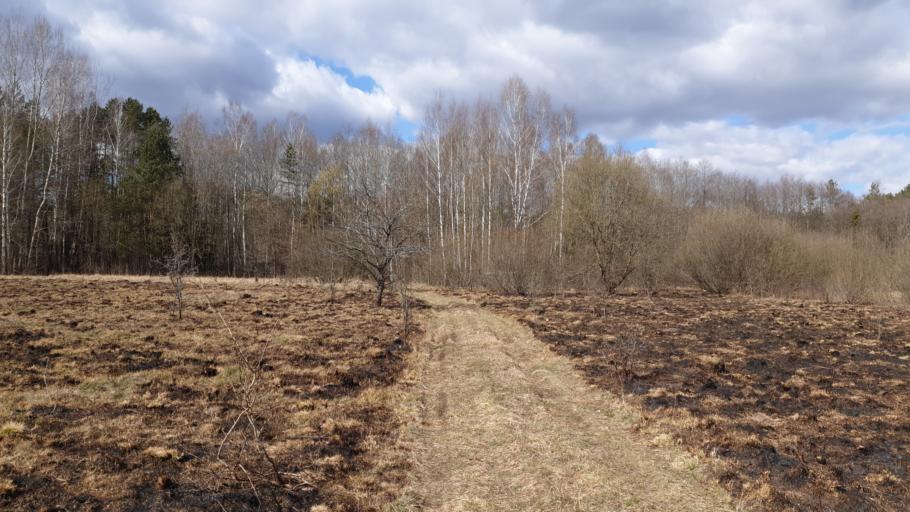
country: LT
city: Grigiskes
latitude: 54.7249
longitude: 25.0265
